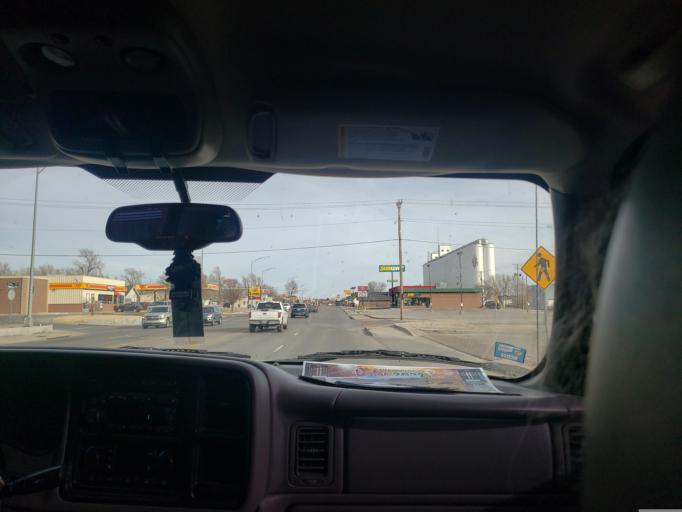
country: US
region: Kansas
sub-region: Ford County
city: Dodge City
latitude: 37.7535
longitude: -100.0299
